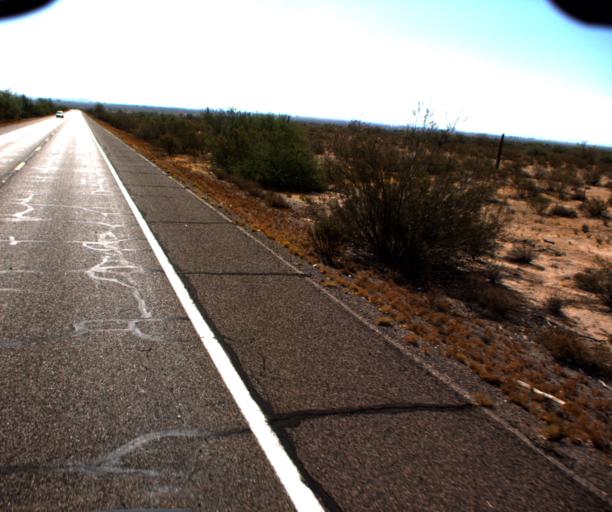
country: US
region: Arizona
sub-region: Pinal County
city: Blackwater
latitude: 33.0184
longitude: -111.6495
